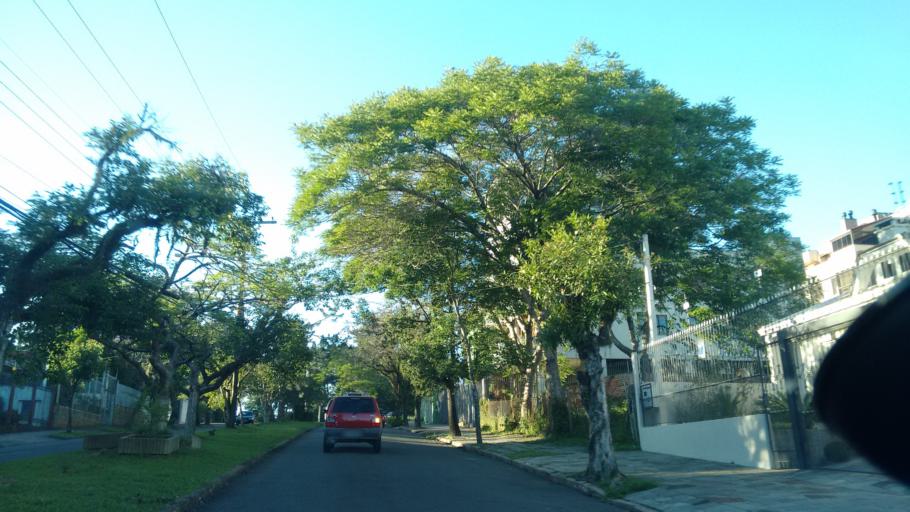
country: BR
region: Rio Grande do Sul
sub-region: Cachoeirinha
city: Cachoeirinha
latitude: -30.0032
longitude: -51.1458
